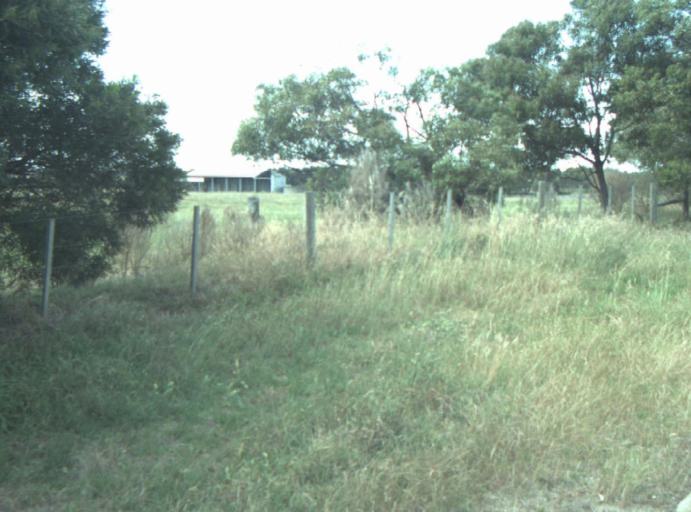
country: AU
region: Victoria
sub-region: Greater Geelong
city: Clifton Springs
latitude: -38.1928
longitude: 144.5670
